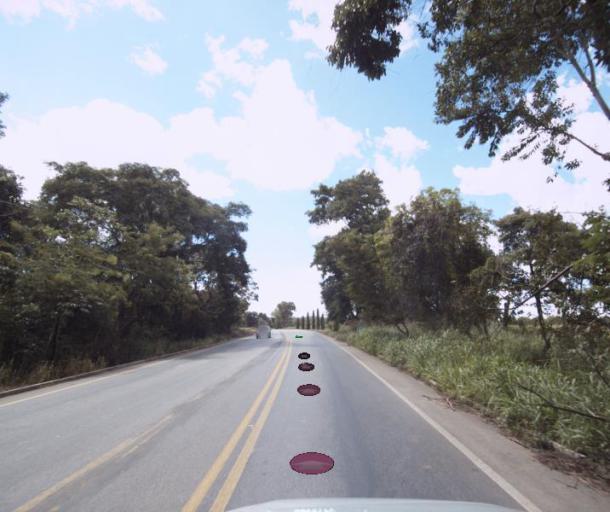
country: BR
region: Goias
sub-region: Porangatu
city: Porangatu
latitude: -13.7611
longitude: -49.0282
